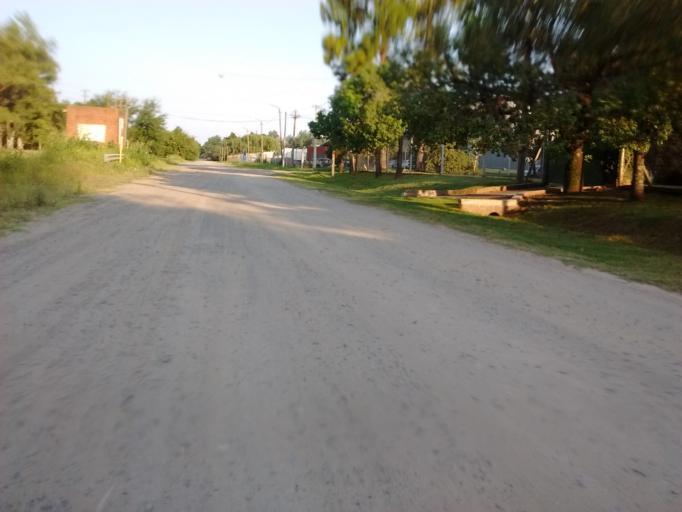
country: AR
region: Santa Fe
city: Funes
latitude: -32.9247
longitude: -60.7573
